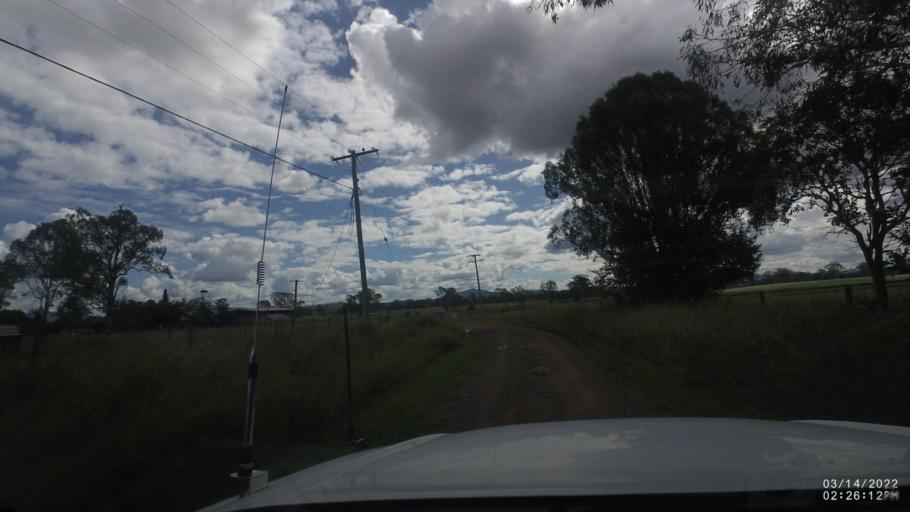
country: AU
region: Queensland
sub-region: Logan
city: Cedar Vale
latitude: -27.9058
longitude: 152.9697
